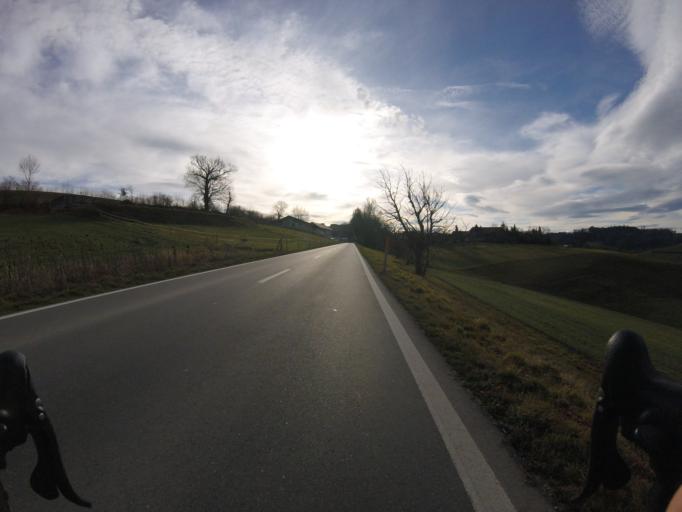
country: CH
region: Fribourg
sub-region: Sense District
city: Ueberstorf
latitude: 46.8595
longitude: 7.3150
